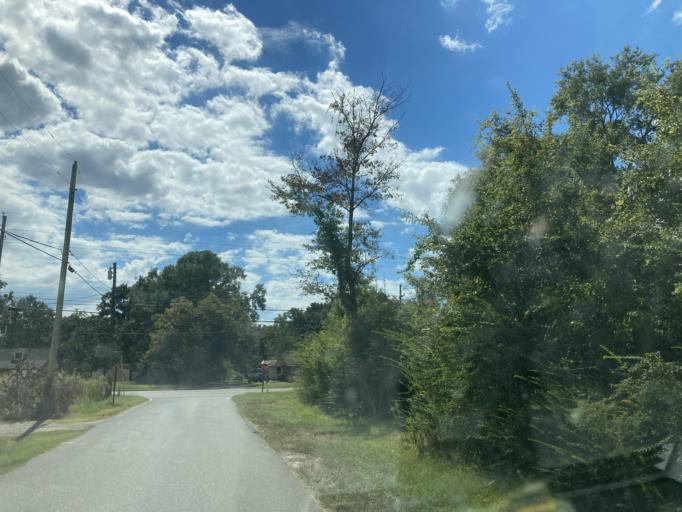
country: US
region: Mississippi
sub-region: Jackson County
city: Gulf Hills
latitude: 30.4438
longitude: -88.8497
